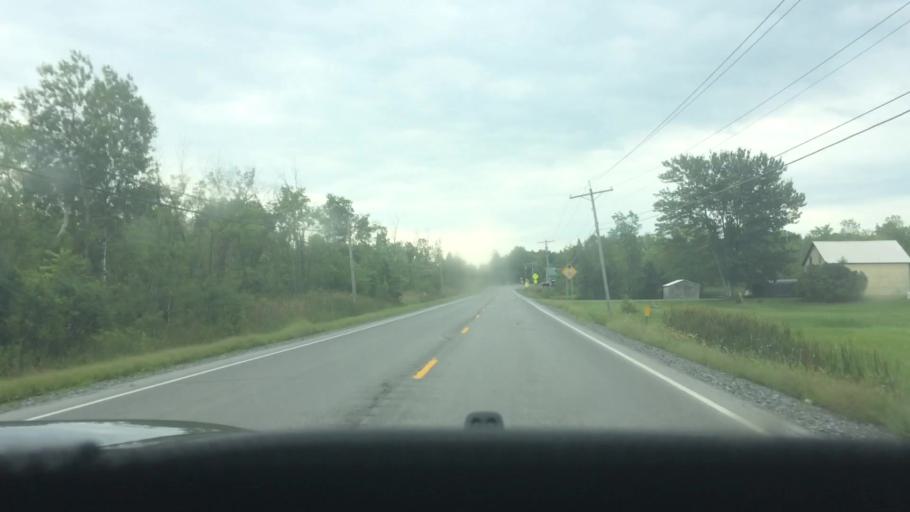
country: US
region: New York
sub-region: St. Lawrence County
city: Ogdensburg
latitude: 44.6252
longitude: -75.4159
